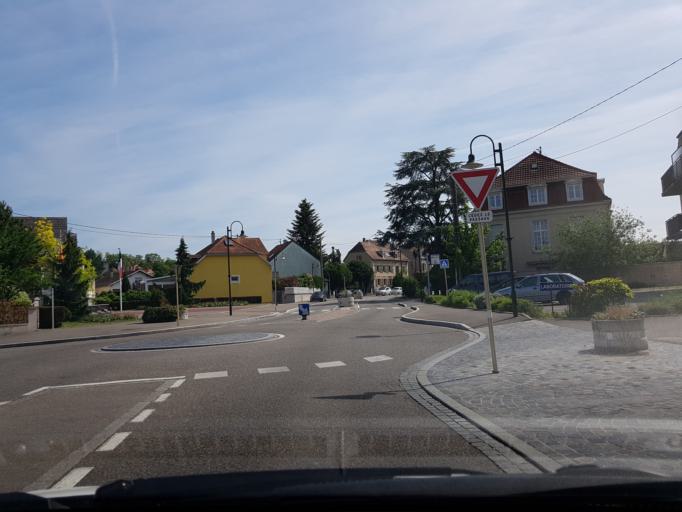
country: FR
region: Alsace
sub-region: Departement du Haut-Rhin
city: Brunstatt
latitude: 47.7243
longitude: 7.3196
